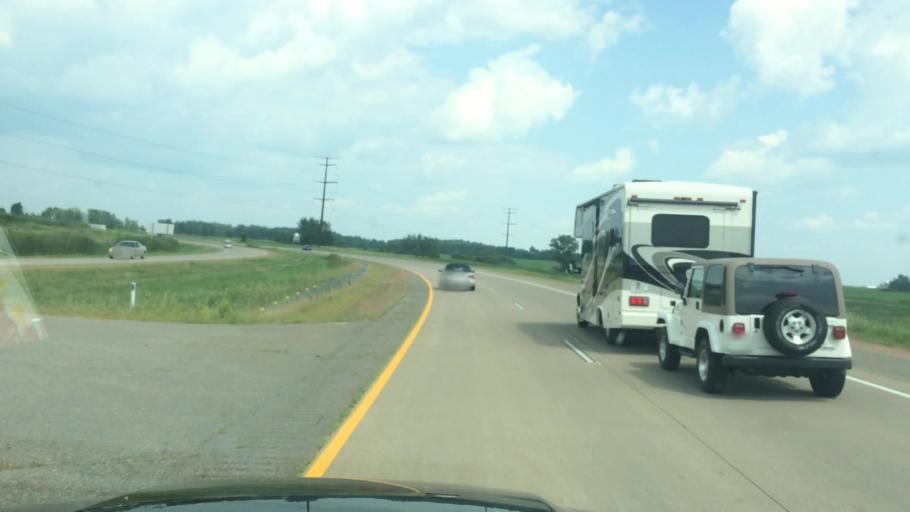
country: US
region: Wisconsin
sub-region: Clark County
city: Abbotsford
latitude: 44.9327
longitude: -90.2985
